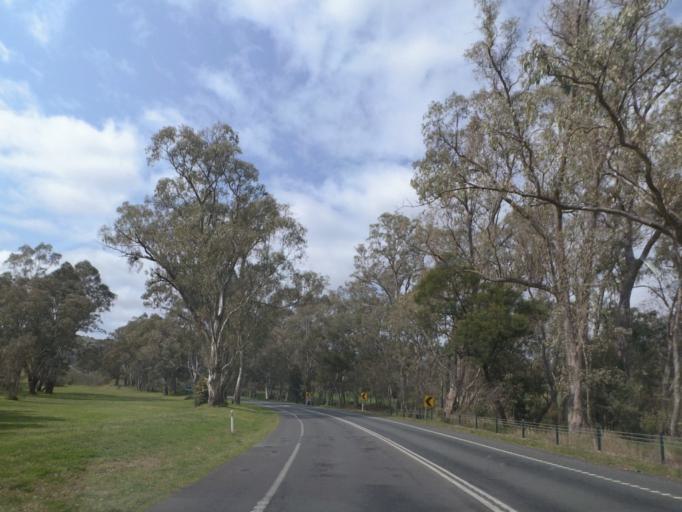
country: AU
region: Victoria
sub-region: Murrindindi
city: Kinglake West
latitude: -37.1212
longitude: 145.2163
